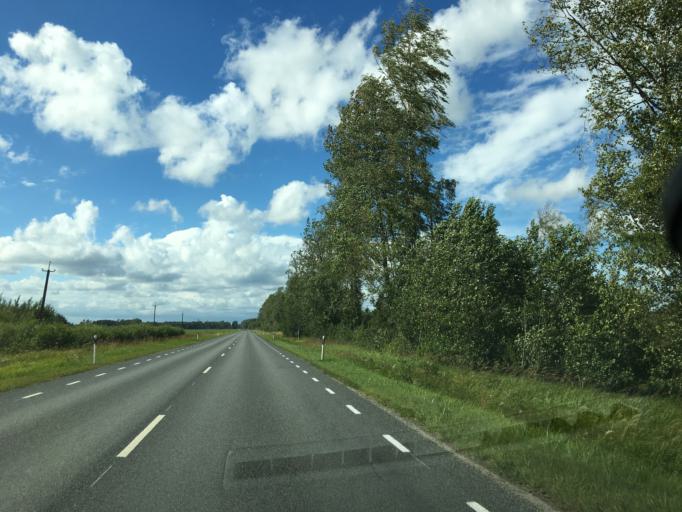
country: EE
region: Paernumaa
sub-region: Vaendra vald (alev)
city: Vandra
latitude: 58.5985
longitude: 25.1431
